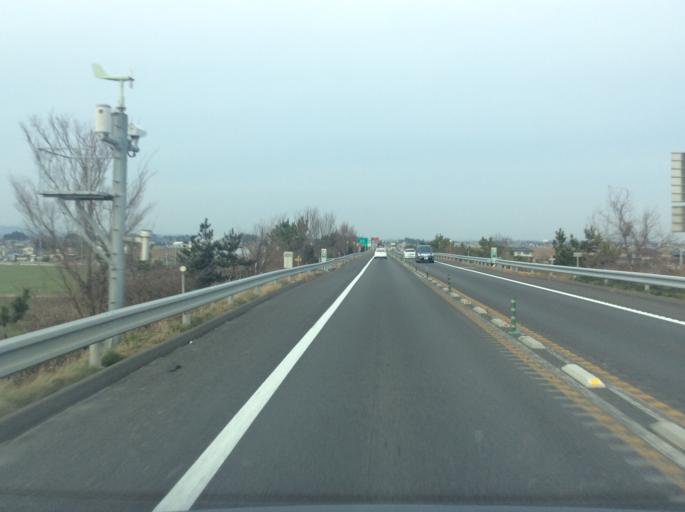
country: JP
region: Miyagi
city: Iwanuma
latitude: 38.0976
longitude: 140.8884
